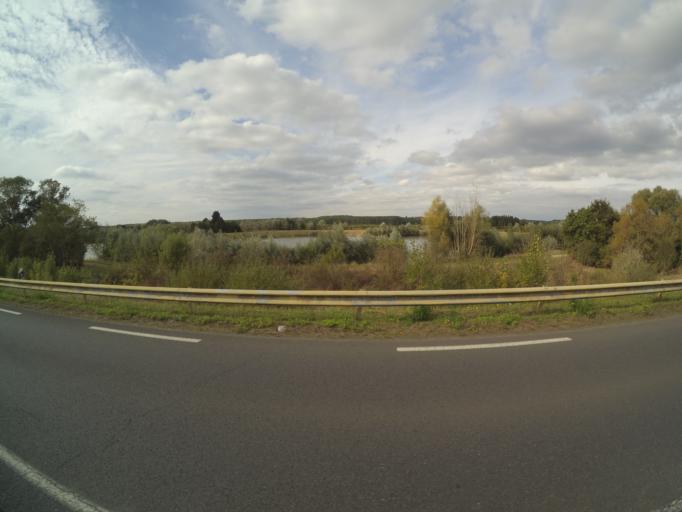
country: FR
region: Centre
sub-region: Departement d'Indre-et-Loire
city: Cinq-Mars-la-Pile
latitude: 47.3343
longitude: 0.4602
